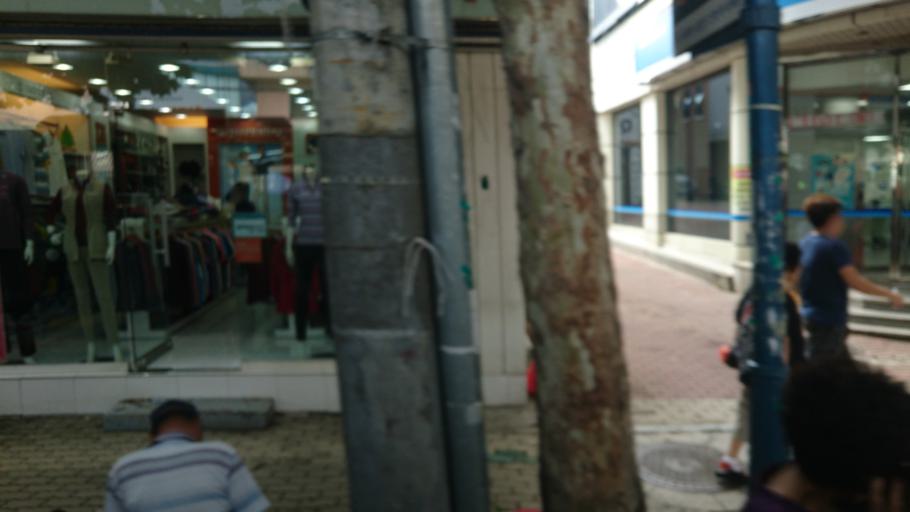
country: KR
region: Daegu
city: Daegu
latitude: 35.8745
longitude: 128.6392
